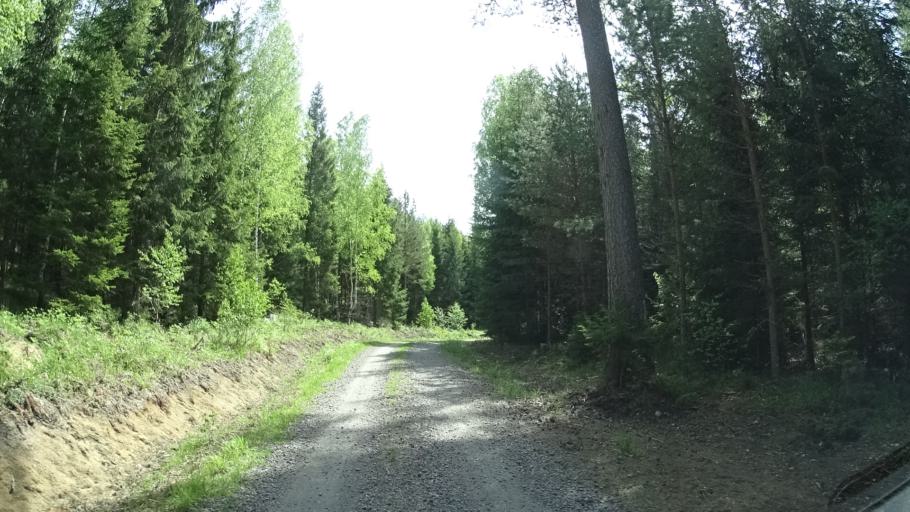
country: SE
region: OEstergoetland
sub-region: Finspangs Kommun
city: Finspang
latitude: 58.8065
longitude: 15.8386
